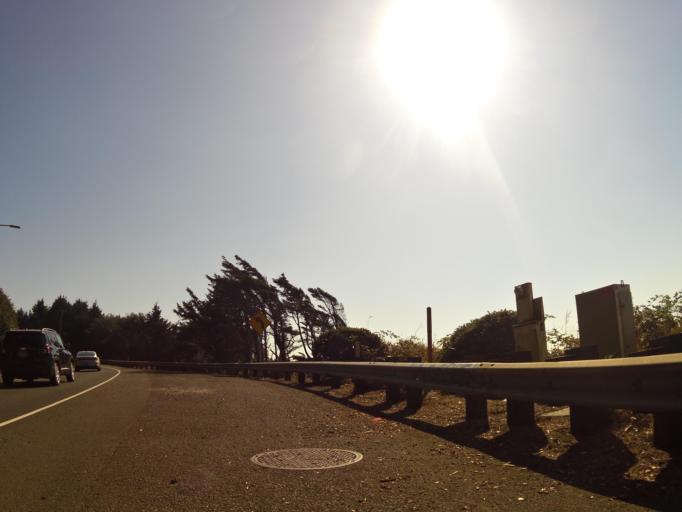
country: US
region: Oregon
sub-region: Clatsop County
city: Cannon Beach
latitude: 45.7984
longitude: -123.9670
